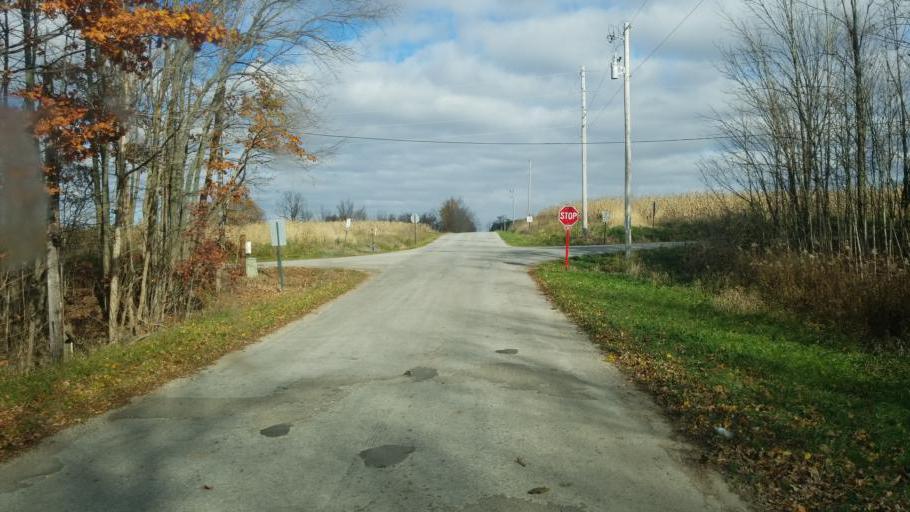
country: US
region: Ohio
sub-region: Crawford County
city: Galion
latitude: 40.6531
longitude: -82.7468
